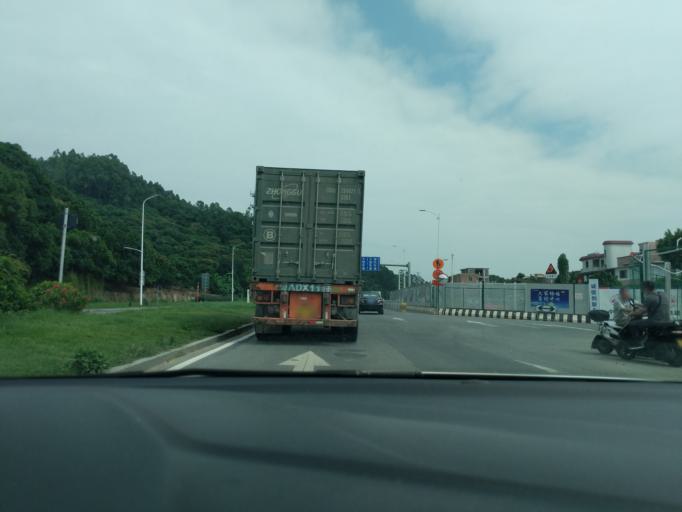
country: CN
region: Guangdong
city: Nansha
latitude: 22.7554
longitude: 113.5704
